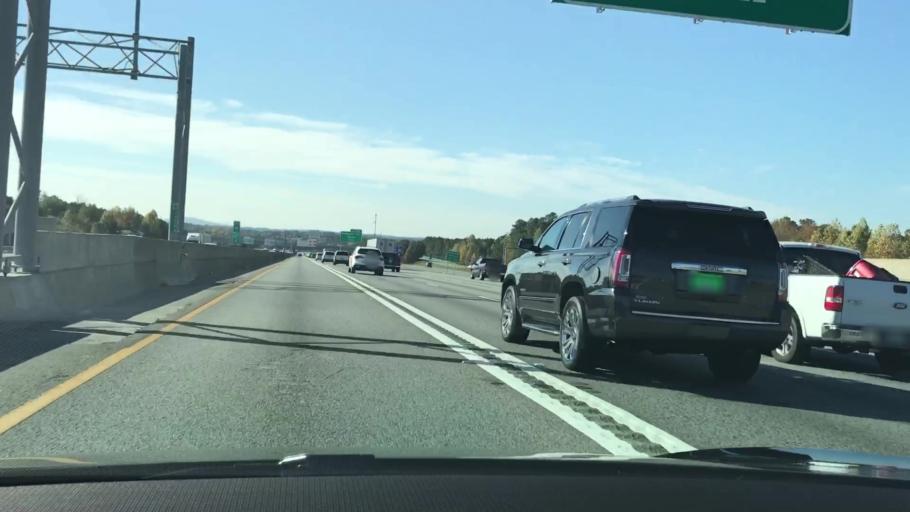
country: US
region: Georgia
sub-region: Gwinnett County
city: Duluth
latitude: 33.9822
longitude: -84.0869
